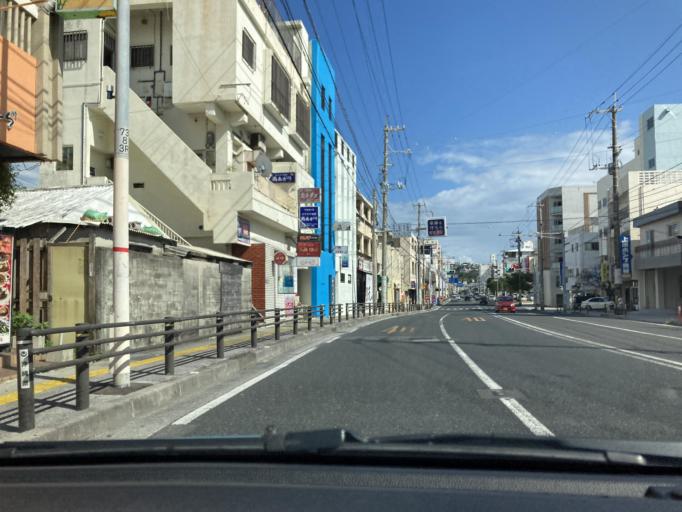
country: JP
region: Okinawa
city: Naha-shi
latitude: 26.1995
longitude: 127.6873
